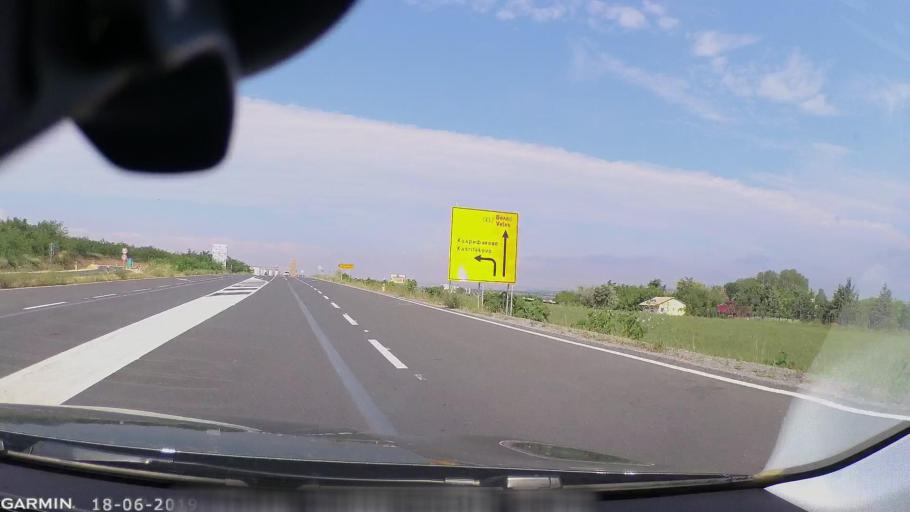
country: MK
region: Sveti Nikole
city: Sveti Nikole
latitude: 41.8255
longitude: 22.0084
